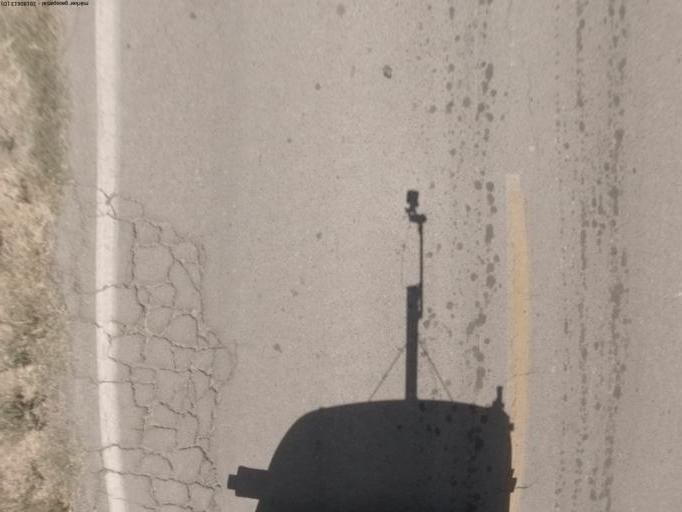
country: US
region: California
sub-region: Madera County
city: Chowchilla
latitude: 37.0180
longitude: -120.3722
